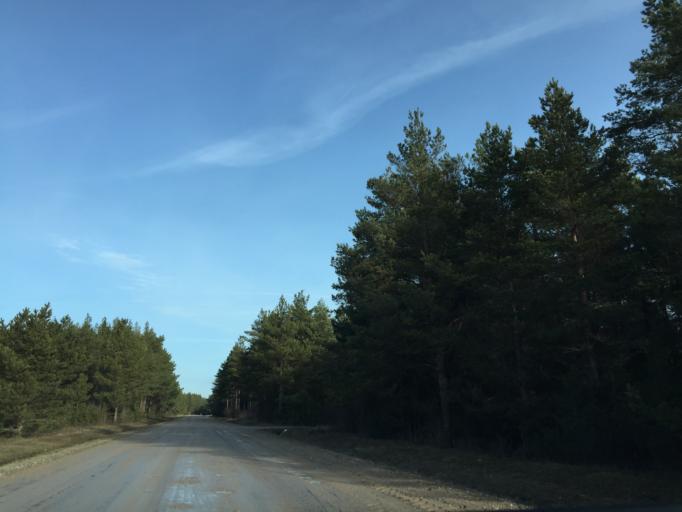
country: EE
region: Saare
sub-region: Kuressaare linn
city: Kuressaare
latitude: 58.2753
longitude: 21.9147
